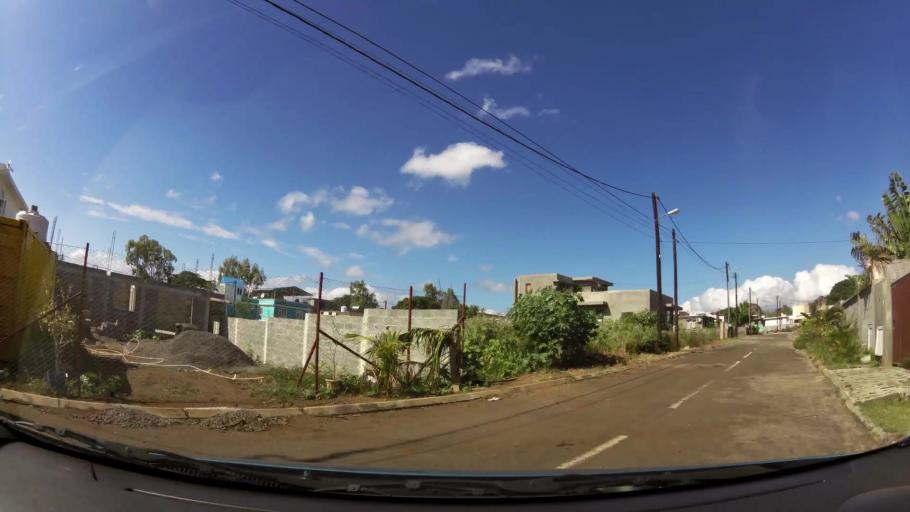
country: MU
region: Black River
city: Gros Cailloux
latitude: -20.2211
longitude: 57.4275
